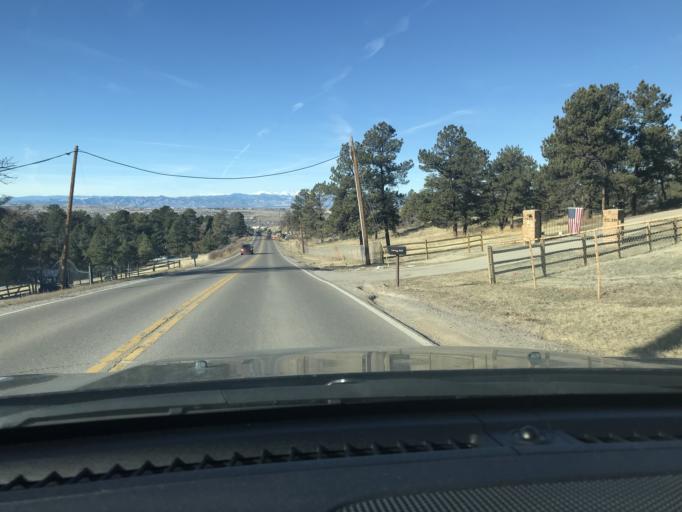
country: US
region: Colorado
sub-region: Douglas County
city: Parker
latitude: 39.5514
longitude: -104.7479
